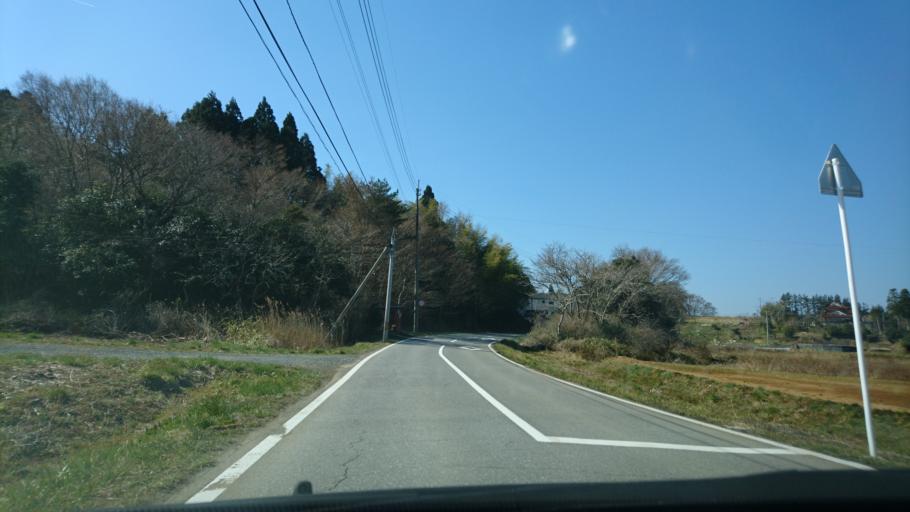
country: JP
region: Iwate
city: Ofunato
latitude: 38.8623
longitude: 141.6095
